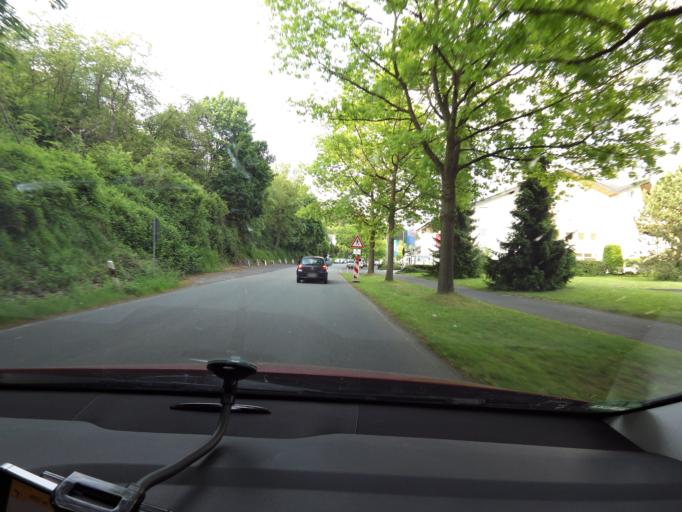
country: DE
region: Hesse
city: Oberbiel
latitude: 50.5539
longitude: 8.4362
